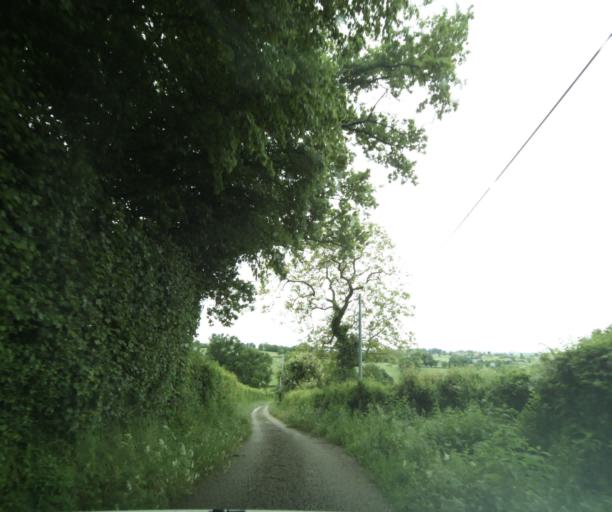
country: FR
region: Bourgogne
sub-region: Departement de Saone-et-Loire
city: La Clayette
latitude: 46.3472
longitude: 4.2138
